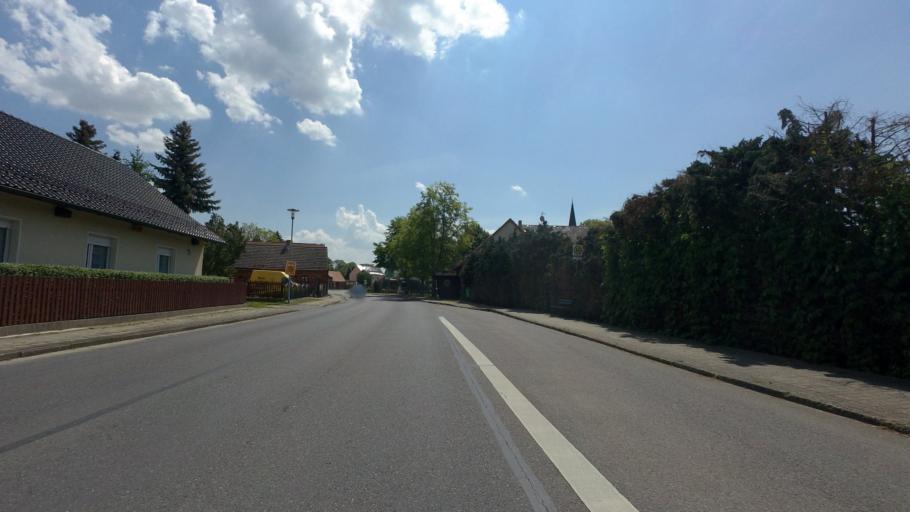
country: DE
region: Brandenburg
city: Neu Zauche
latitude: 51.9292
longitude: 14.0898
